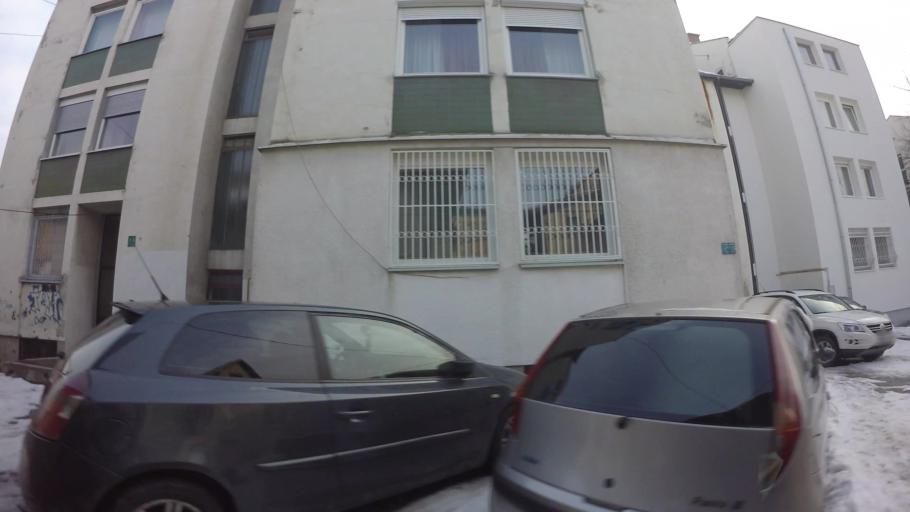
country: BA
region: Federation of Bosnia and Herzegovina
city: Kobilja Glava
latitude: 43.8623
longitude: 18.4263
